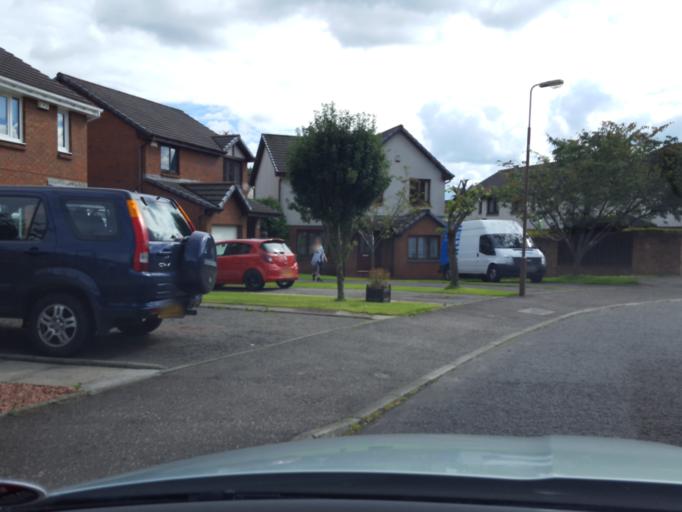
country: GB
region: Scotland
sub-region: West Lothian
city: Livingston
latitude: 55.9028
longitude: -3.5370
